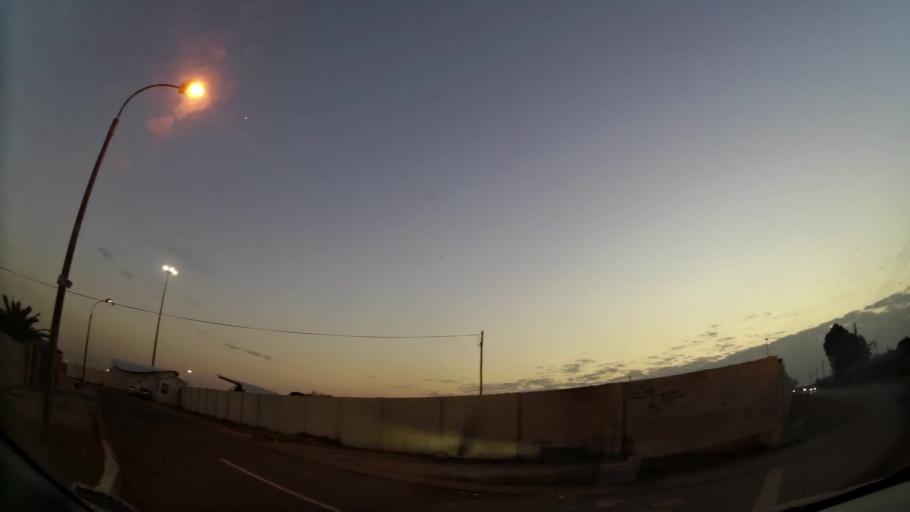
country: ZA
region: Gauteng
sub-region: West Rand District Municipality
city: Randfontein
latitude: -26.2052
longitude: 27.7108
